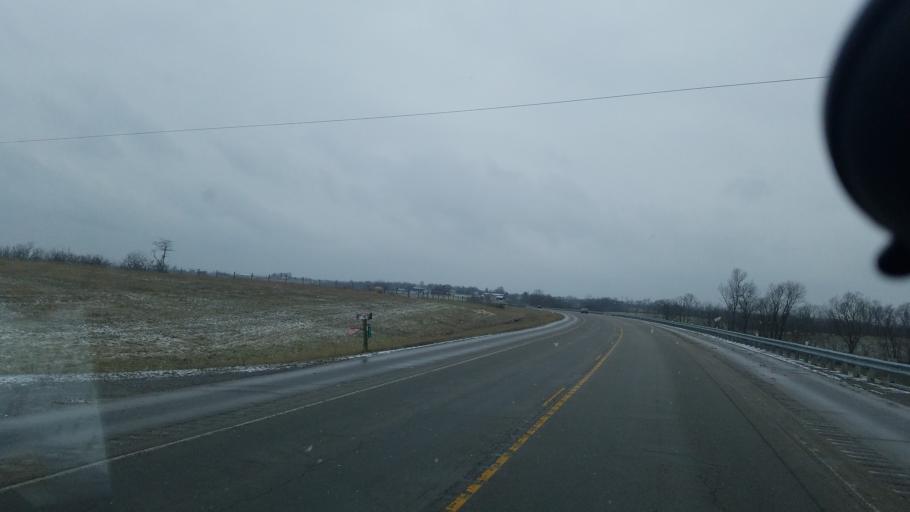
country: US
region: Kentucky
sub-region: Bath County
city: Owingsville
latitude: 38.2620
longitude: -83.8450
